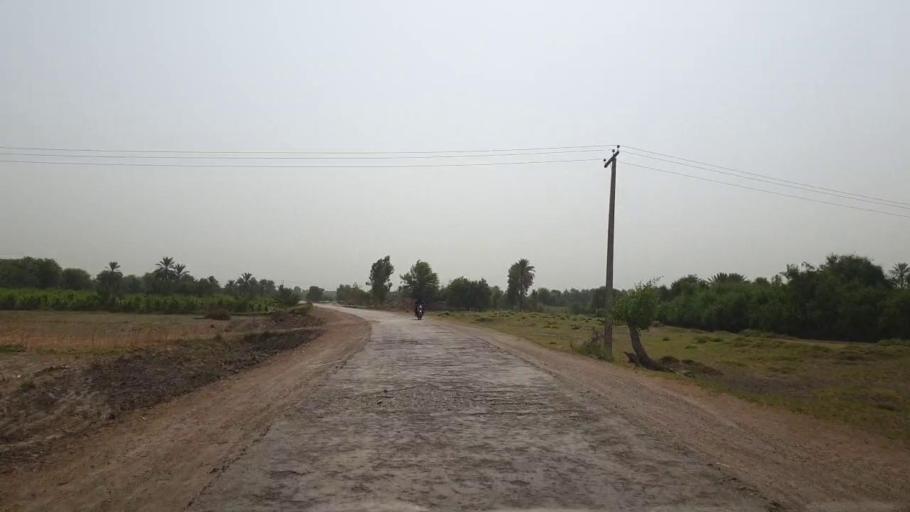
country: PK
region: Sindh
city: Gambat
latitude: 27.4317
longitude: 68.5291
